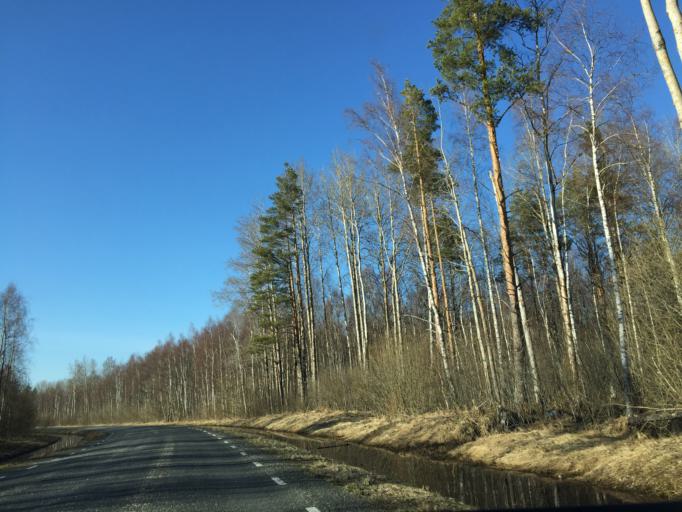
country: RU
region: Pskov
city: Gdov
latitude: 59.0035
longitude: 27.6936
